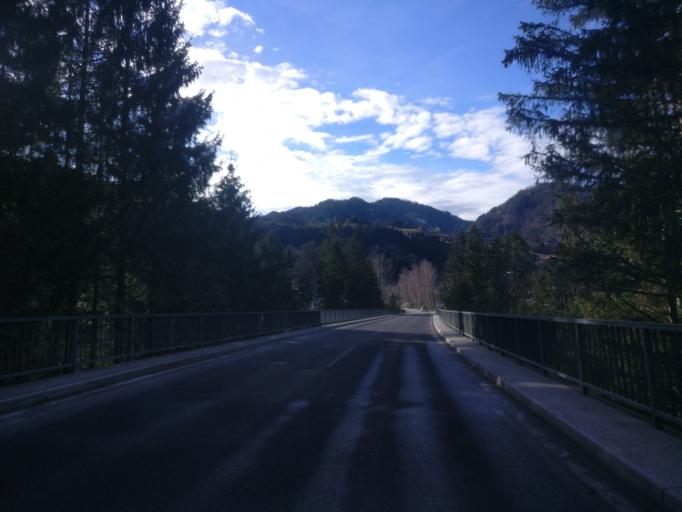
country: AT
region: Styria
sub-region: Politischer Bezirk Liezen
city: Sankt Gallen
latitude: 47.6849
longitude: 14.6216
